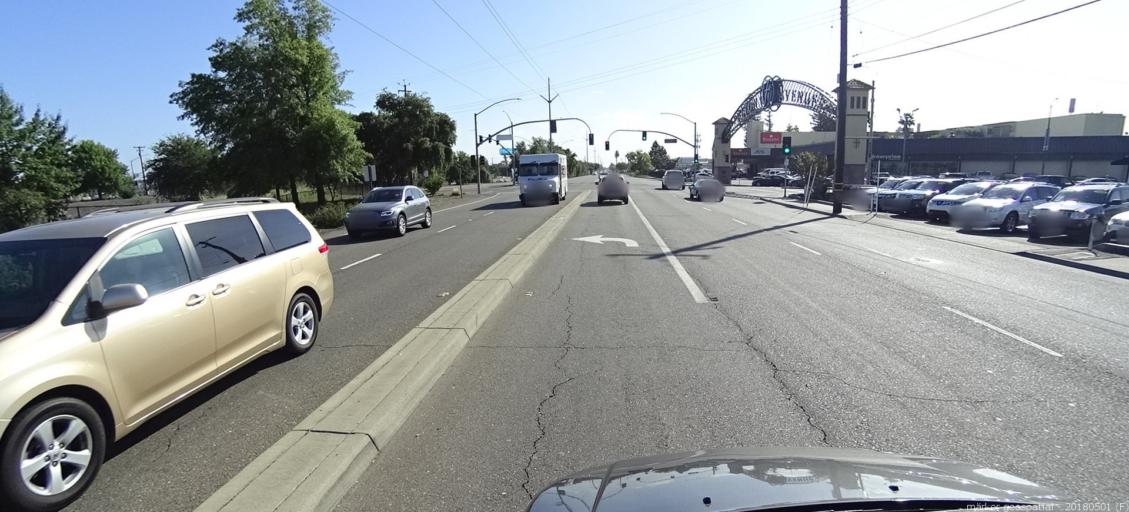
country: US
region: California
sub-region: Sacramento County
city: Arden-Arcade
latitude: 38.6298
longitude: -121.4022
